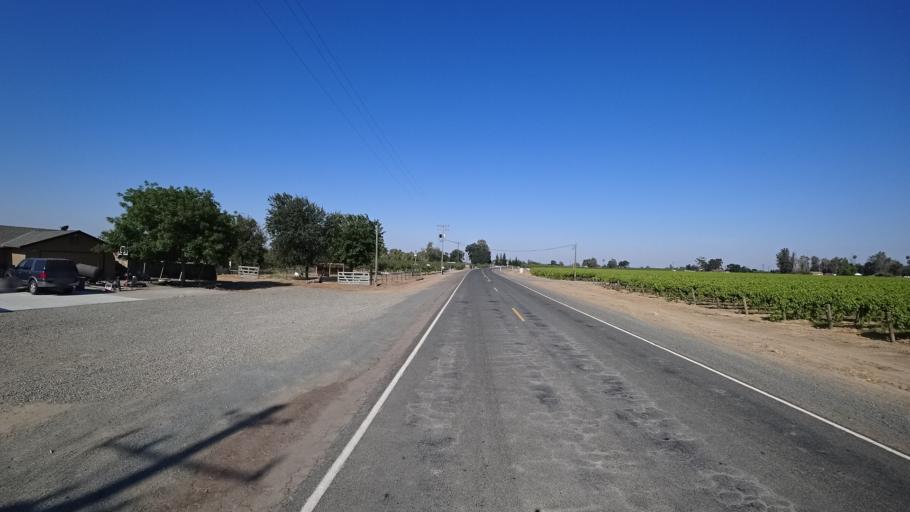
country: US
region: California
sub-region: Kings County
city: Lemoore
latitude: 36.3654
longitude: -119.8214
